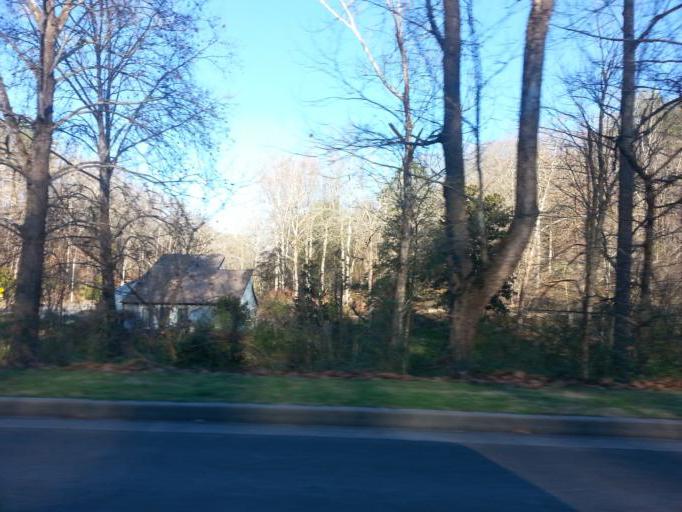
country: US
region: Tennessee
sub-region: Anderson County
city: Oak Ridge
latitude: 35.9931
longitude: -84.2206
